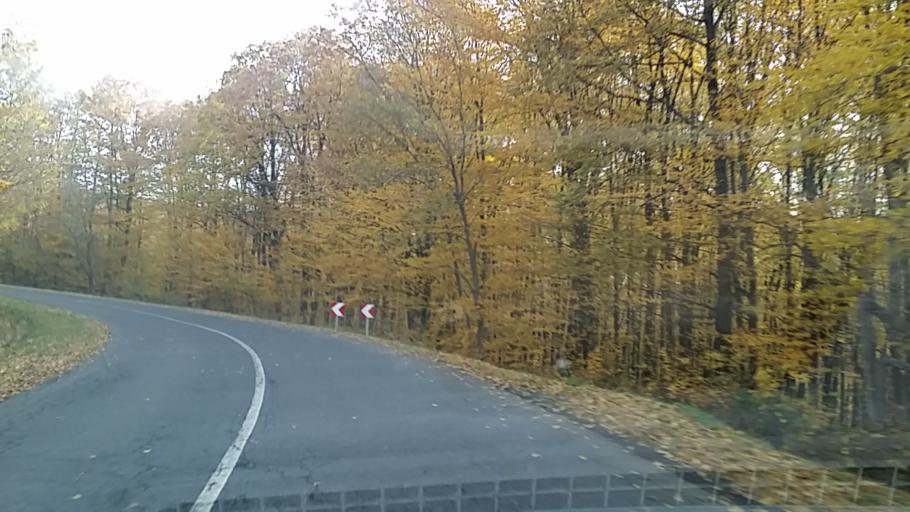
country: HU
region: Borsod-Abauj-Zemplen
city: Gonc
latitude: 48.5407
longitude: 21.3788
